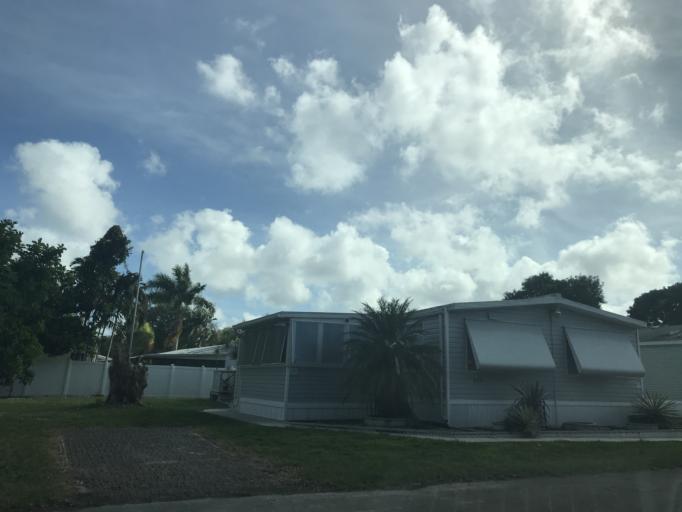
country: US
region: Florida
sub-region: Palm Beach County
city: Boca Pointe
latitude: 26.3124
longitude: -80.1748
